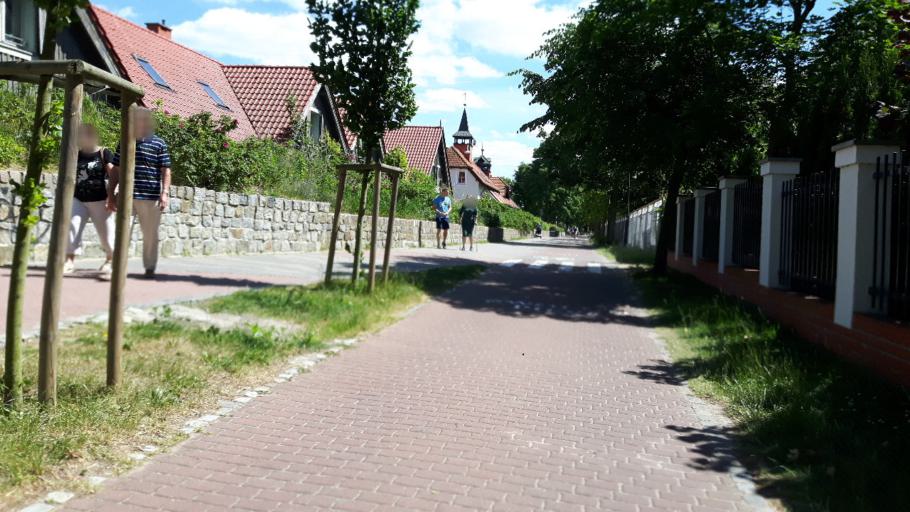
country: PL
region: Pomeranian Voivodeship
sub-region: Sopot
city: Sopot
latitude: 54.4376
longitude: 18.5791
